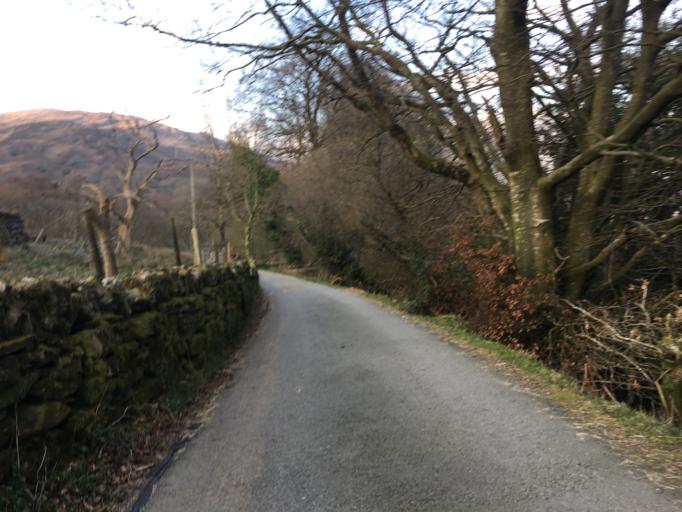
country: GB
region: Wales
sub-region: Gwynedd
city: Porthmadog
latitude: 53.0119
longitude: -4.1115
